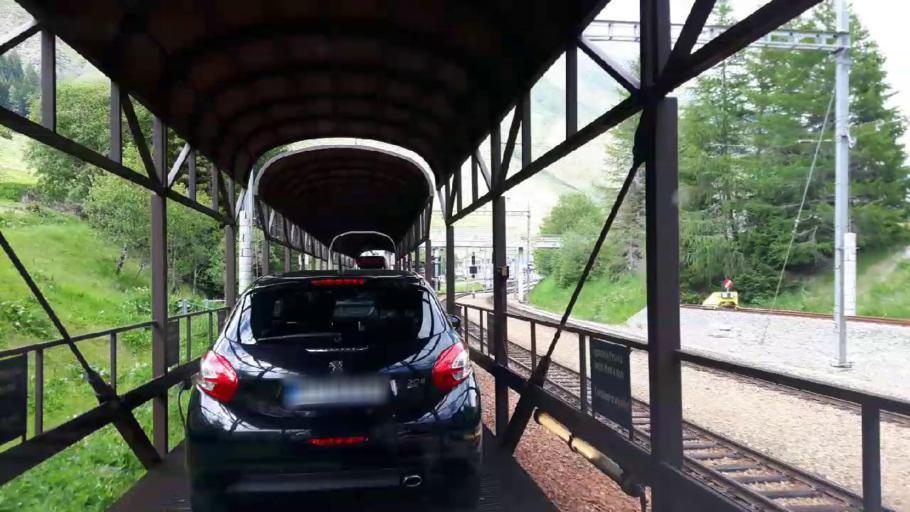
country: CH
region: Uri
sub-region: Uri
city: Andermatt
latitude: 46.5960
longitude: 8.5018
